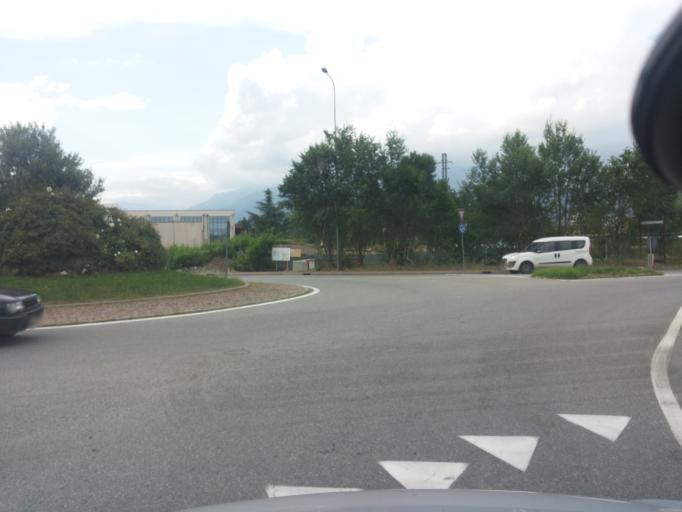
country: IT
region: Piedmont
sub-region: Provincia di Torino
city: Ivrea
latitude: 45.4596
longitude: 7.8843
